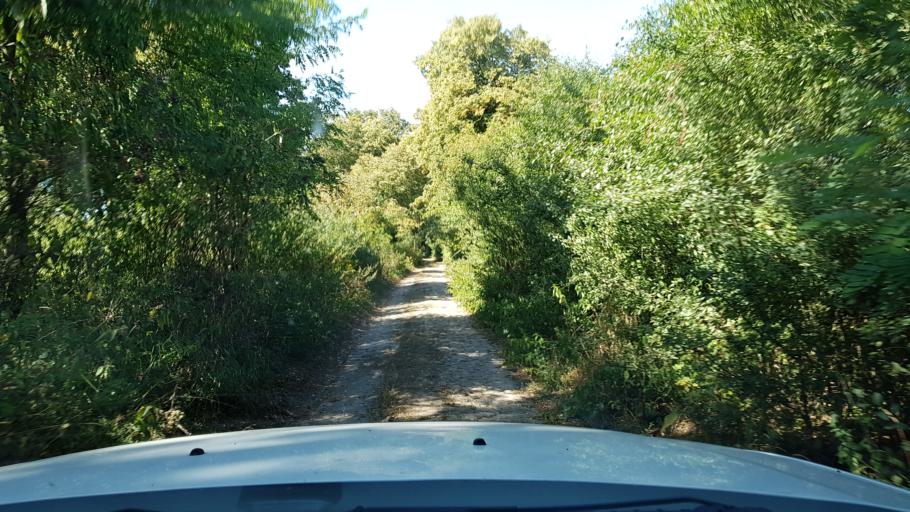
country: PL
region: West Pomeranian Voivodeship
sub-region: Powiat gryfinski
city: Cedynia
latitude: 52.8565
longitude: 14.2256
